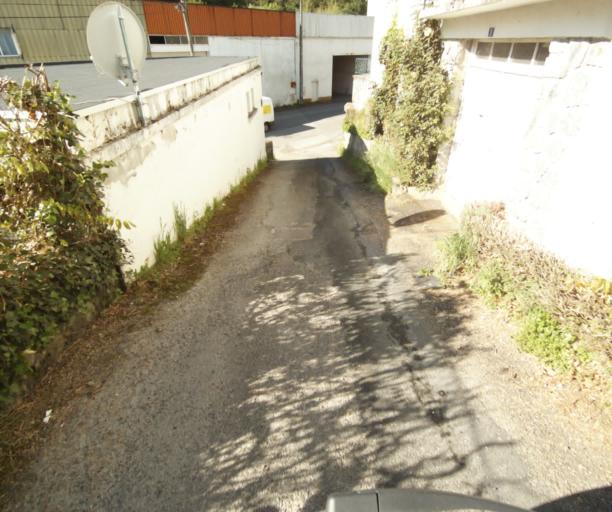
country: FR
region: Limousin
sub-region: Departement de la Correze
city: Tulle
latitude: 45.2756
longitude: 1.7791
